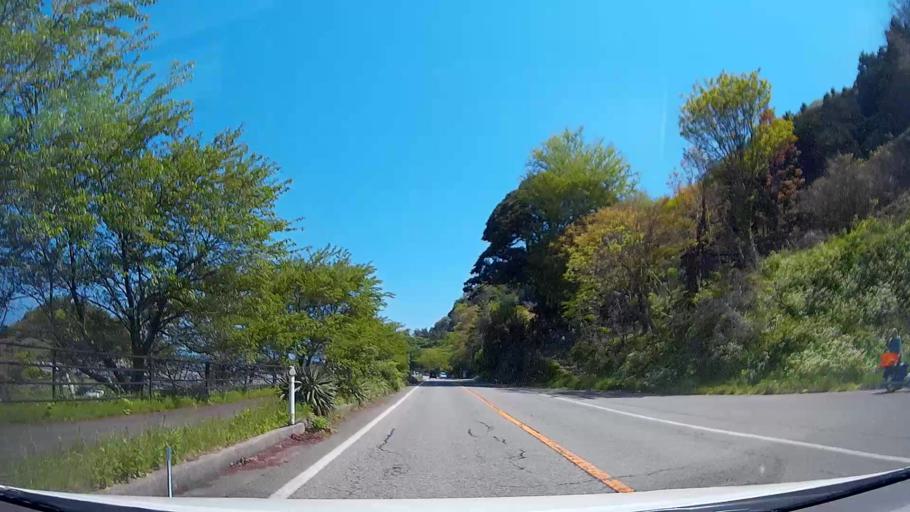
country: JP
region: Ishikawa
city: Nanao
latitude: 37.4136
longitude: 136.9776
